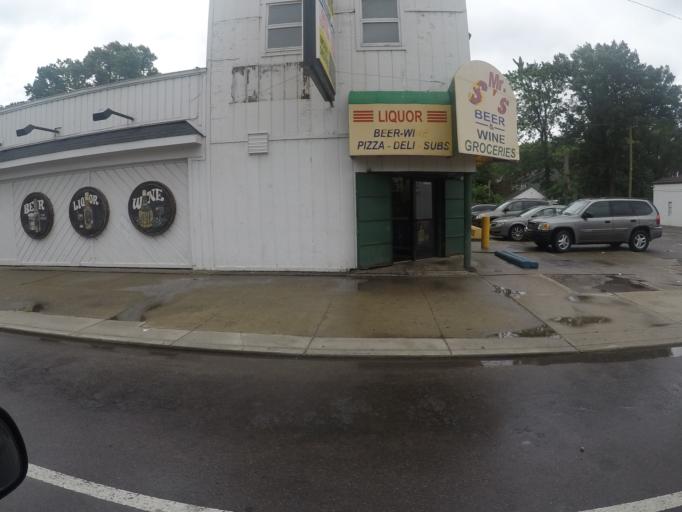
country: US
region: Michigan
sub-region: Wayne County
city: Grosse Pointe
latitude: 42.4050
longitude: -82.9326
